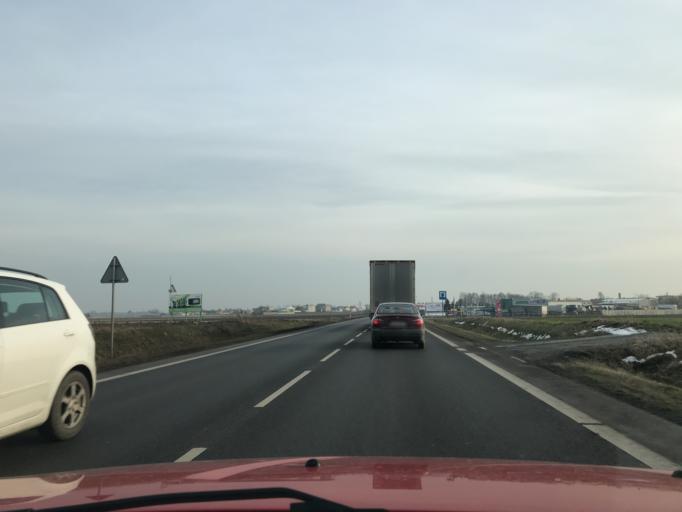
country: PL
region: Greater Poland Voivodeship
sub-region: Powiat pleszewski
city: Pleszew
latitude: 51.8982
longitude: 17.8022
